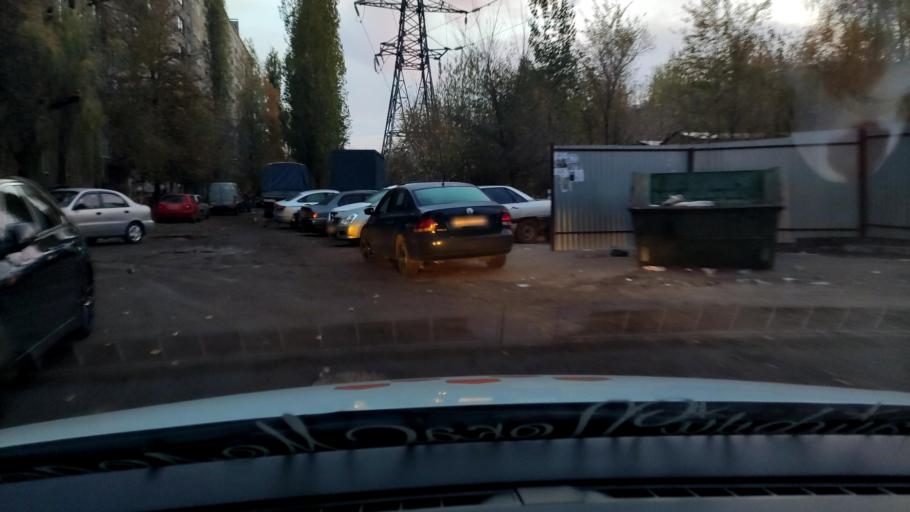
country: RU
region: Voronezj
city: Voronezh
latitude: 51.6798
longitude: 39.1323
